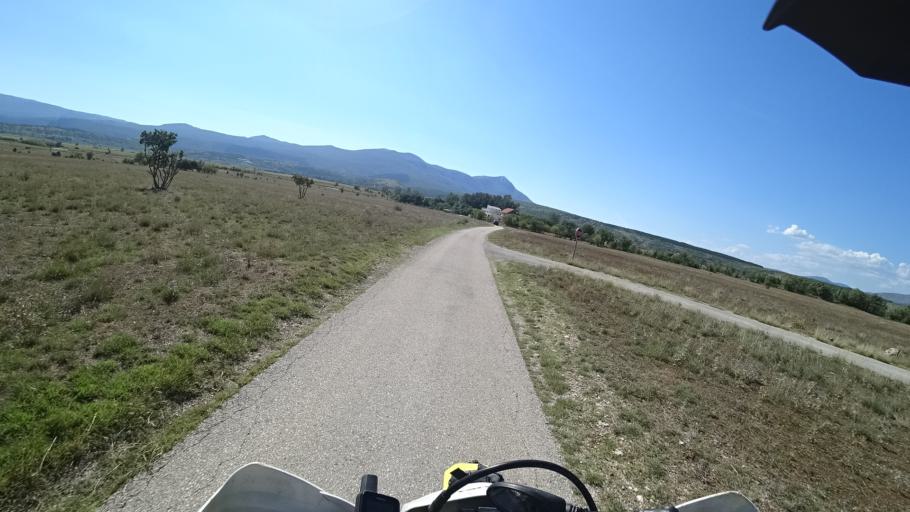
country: BA
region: Federation of Bosnia and Herzegovina
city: Bosansko Grahovo
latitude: 43.9600
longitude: 16.4343
